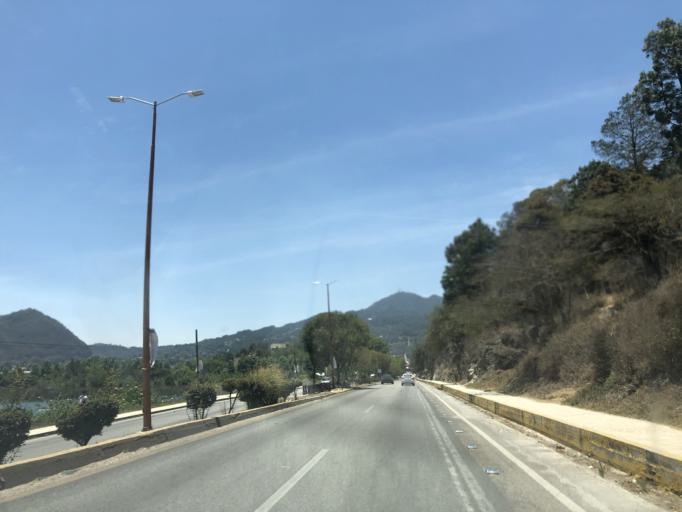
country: MX
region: Chiapas
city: San Cristobal de las Casas
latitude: 16.7314
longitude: -92.6457
